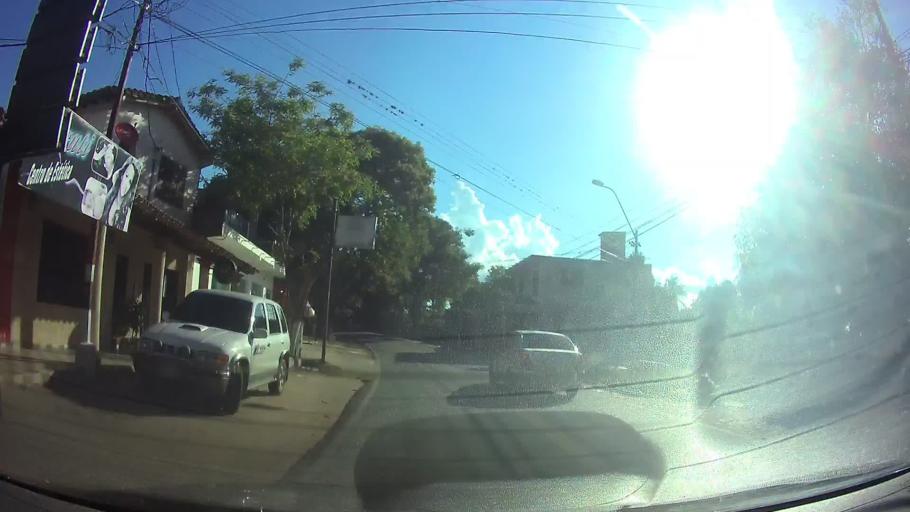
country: PY
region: Central
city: Aregua
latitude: -25.3158
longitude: -57.3879
